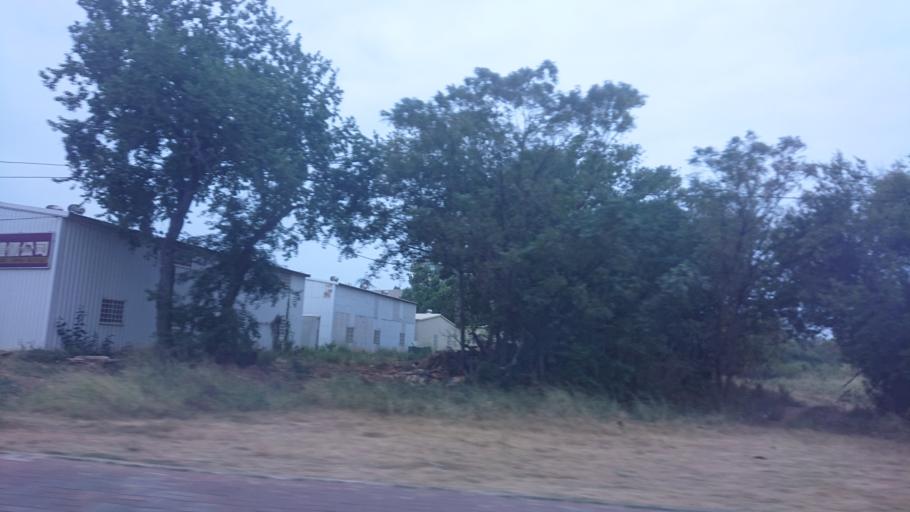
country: TW
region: Fukien
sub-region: Kinmen
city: Jincheng
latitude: 24.4367
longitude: 118.3124
